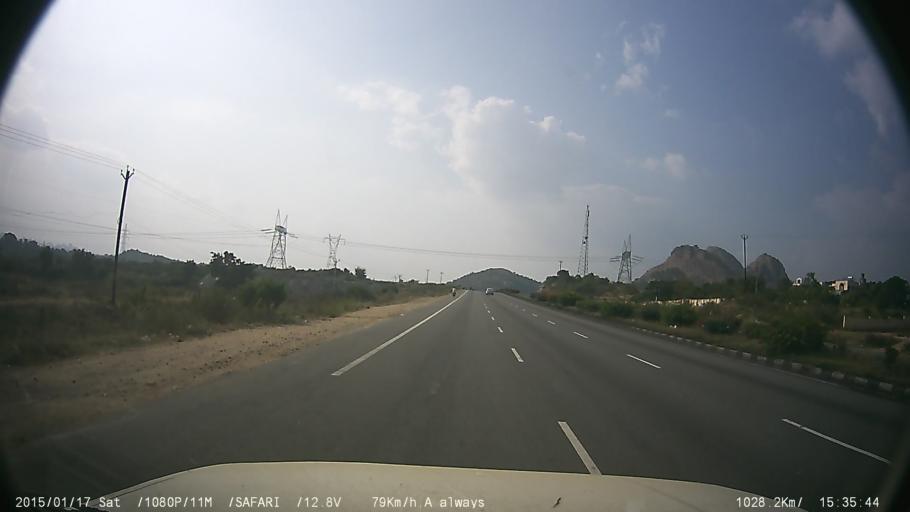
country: IN
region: Tamil Nadu
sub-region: Krishnagiri
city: Kelamangalam
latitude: 12.6517
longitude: 78.0308
